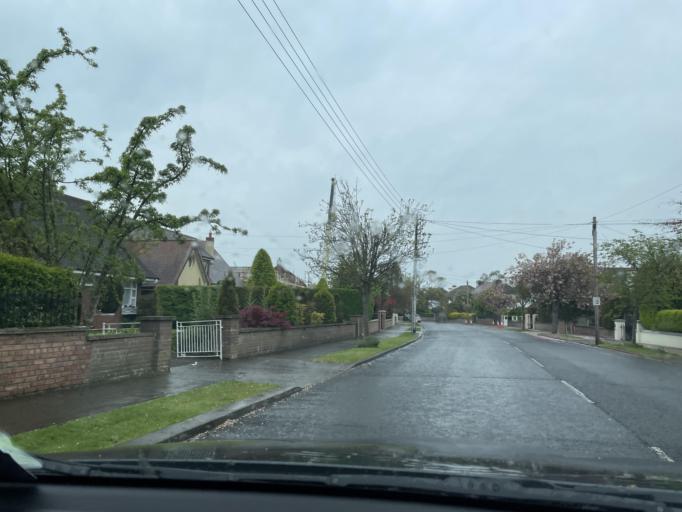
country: IE
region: Leinster
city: Rathgar
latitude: 53.2995
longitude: -6.2703
